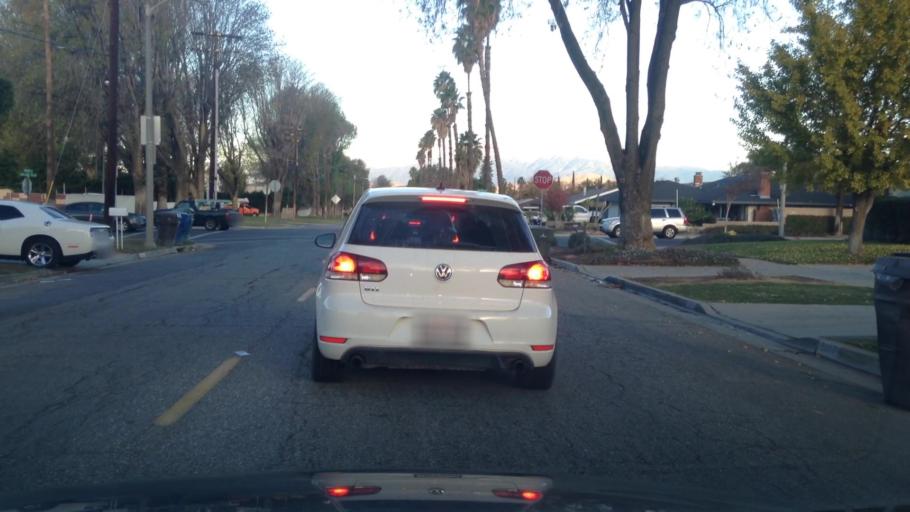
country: US
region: California
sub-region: Riverside County
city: Riverside
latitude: 33.9329
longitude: -117.3916
